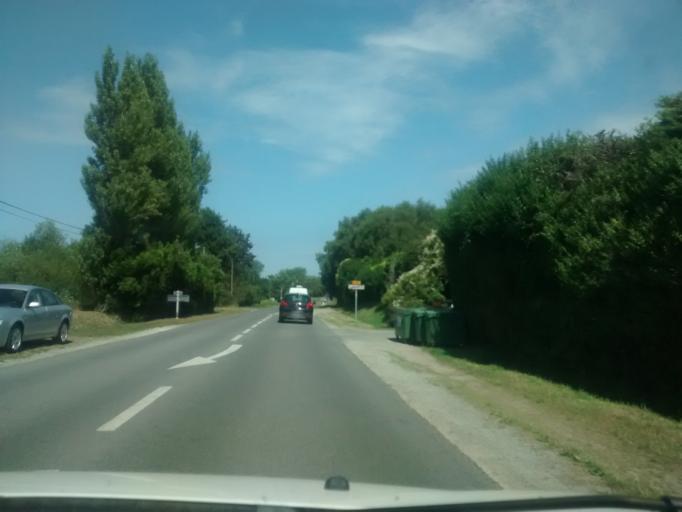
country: FR
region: Brittany
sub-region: Departement d'Ille-et-Vilaine
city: Cancale
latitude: 48.6842
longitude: -1.8555
